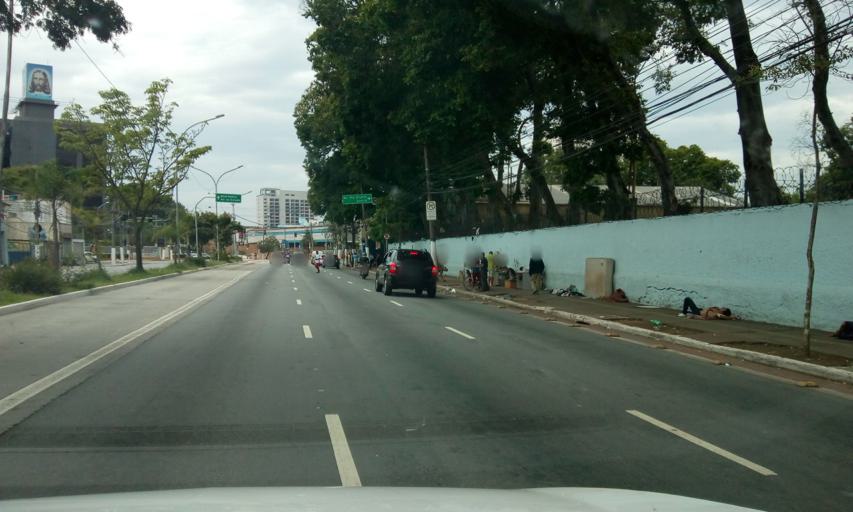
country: BR
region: Sao Paulo
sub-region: Sao Paulo
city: Sao Paulo
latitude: -23.5232
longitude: -46.6520
